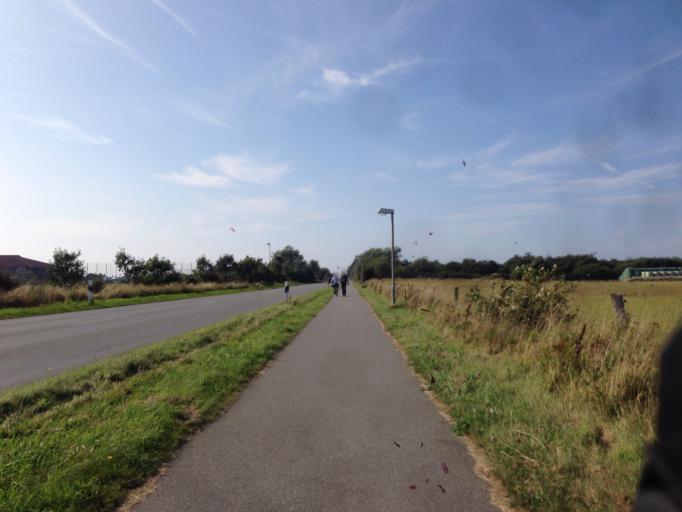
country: DE
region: Schleswig-Holstein
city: Keitum
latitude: 54.8976
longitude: 8.3570
